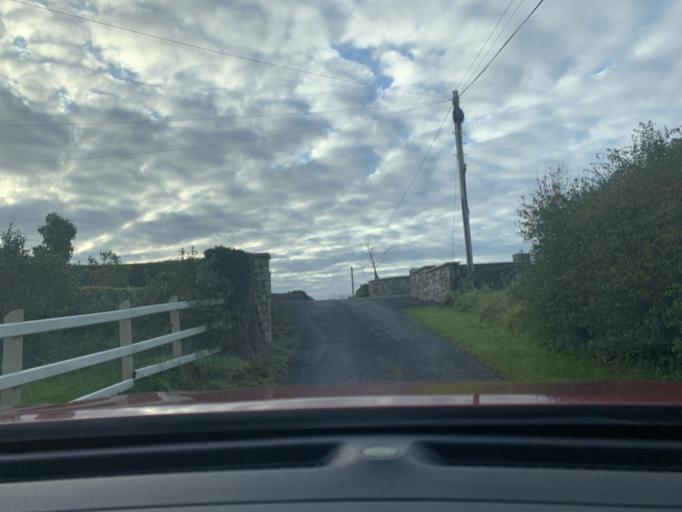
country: IE
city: Ballisodare
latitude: 54.2308
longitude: -8.5123
